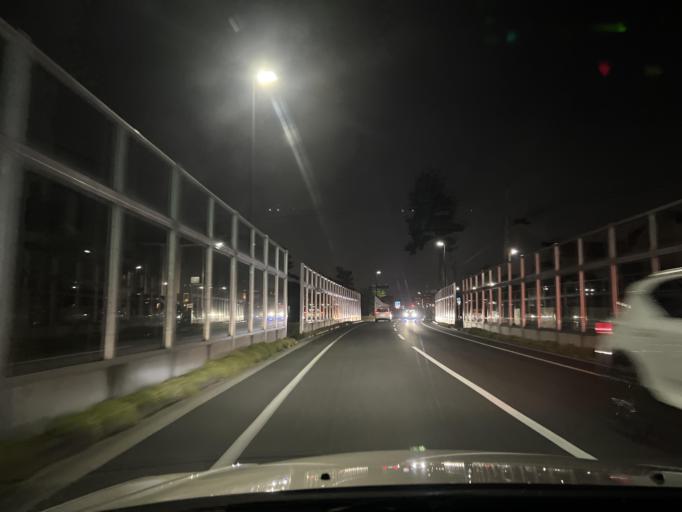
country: JP
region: Chiba
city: Funabashi
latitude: 35.7230
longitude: 139.9362
